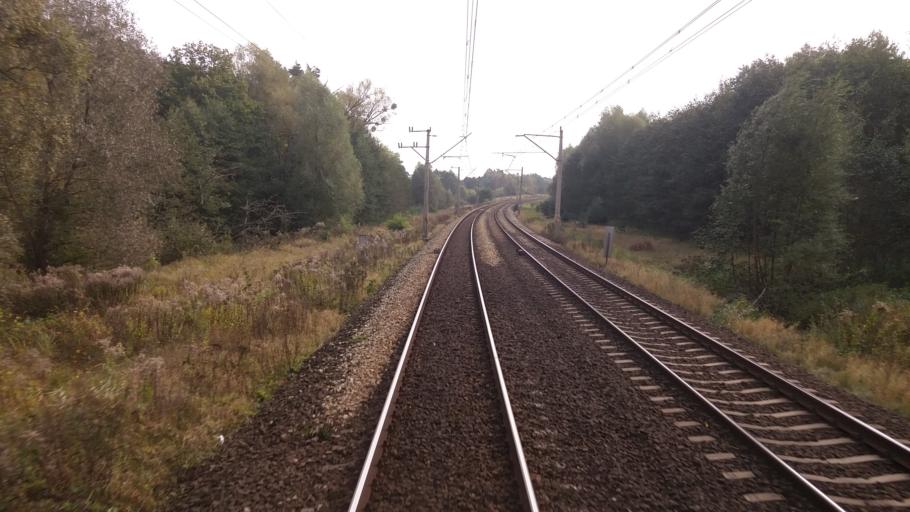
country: PL
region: West Pomeranian Voivodeship
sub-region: Powiat stargardzki
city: Dolice
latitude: 53.1819
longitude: 15.2725
